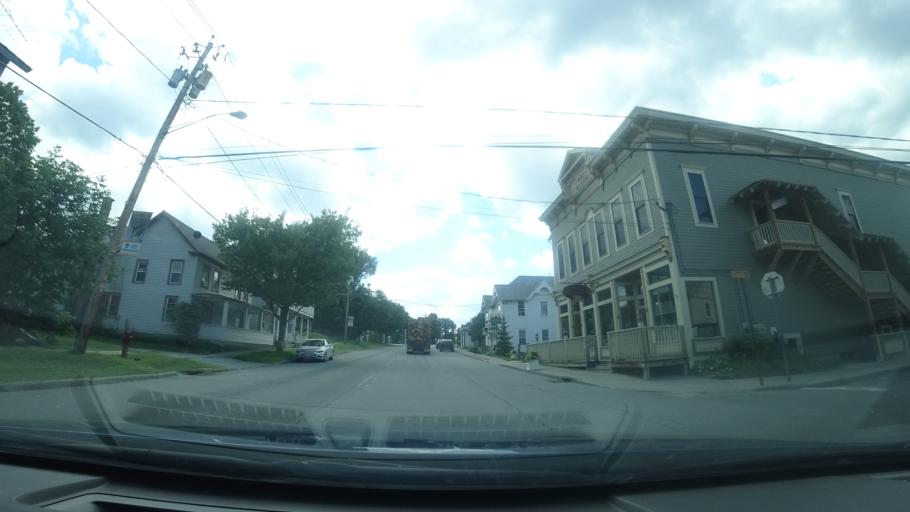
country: US
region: New York
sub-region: Warren County
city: Warrensburg
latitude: 43.6541
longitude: -73.8010
